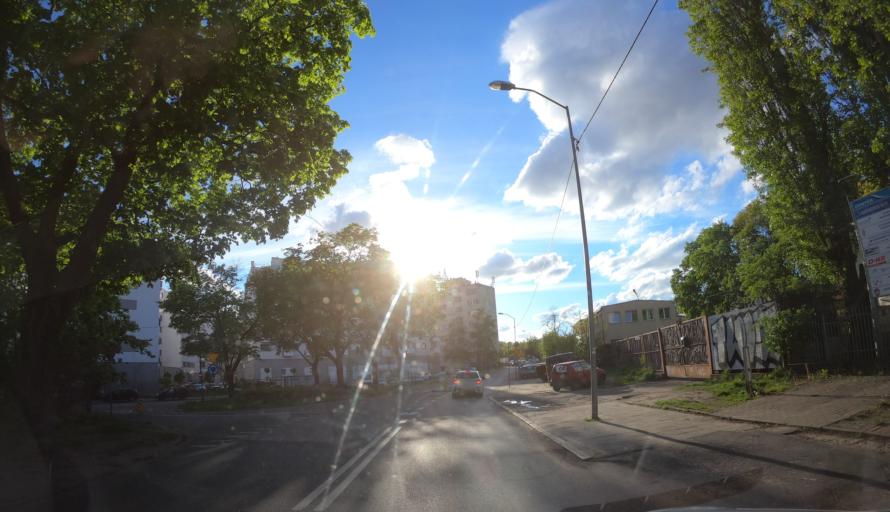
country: PL
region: West Pomeranian Voivodeship
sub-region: Szczecin
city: Szczecin
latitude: 53.4159
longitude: 14.5345
